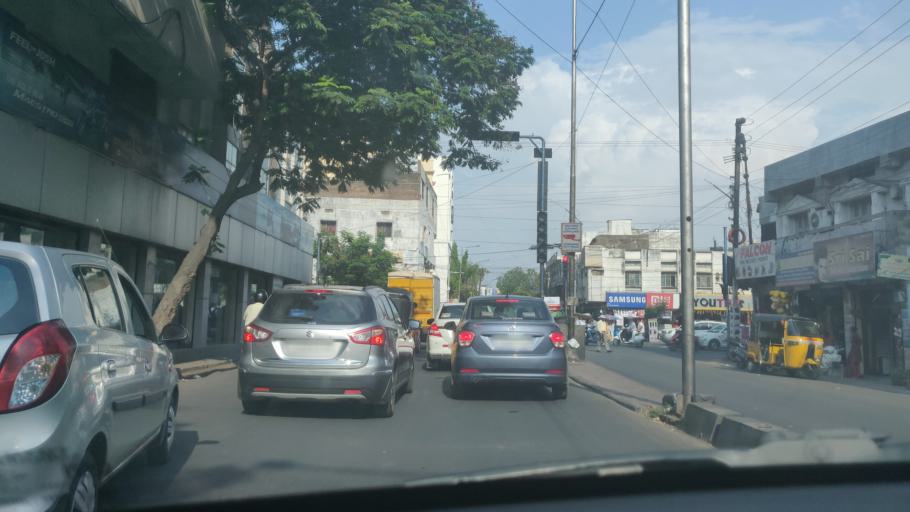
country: IN
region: Telangana
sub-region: Rangareddi
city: Gaddi Annaram
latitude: 17.3940
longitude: 78.5105
